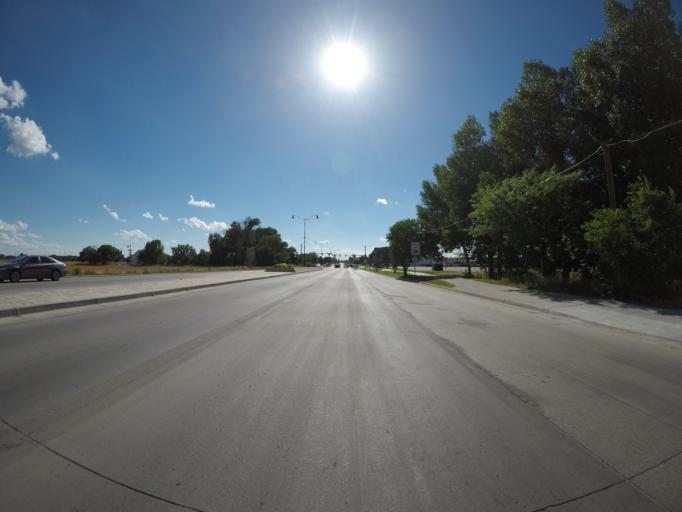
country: US
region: Colorado
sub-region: Logan County
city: Sterling
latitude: 40.6252
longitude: -103.2334
